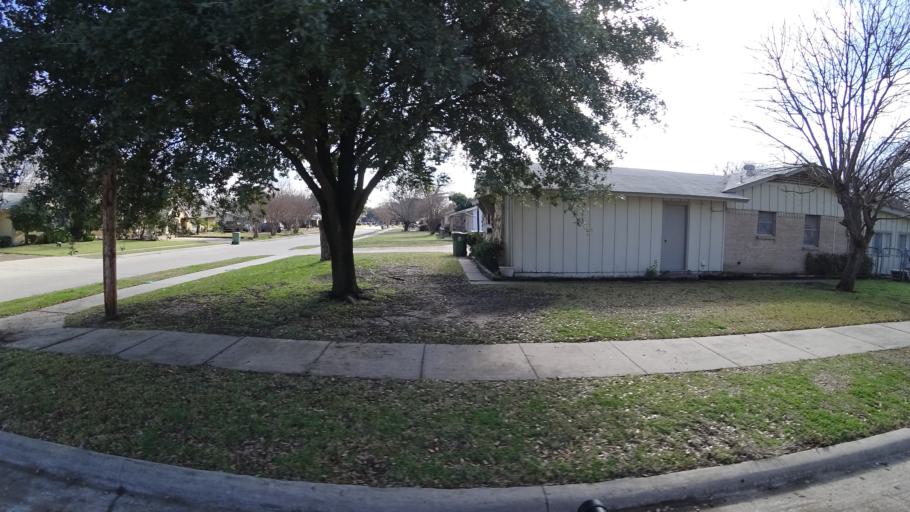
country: US
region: Texas
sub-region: Denton County
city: Lewisville
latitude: 33.0317
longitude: -97.0000
